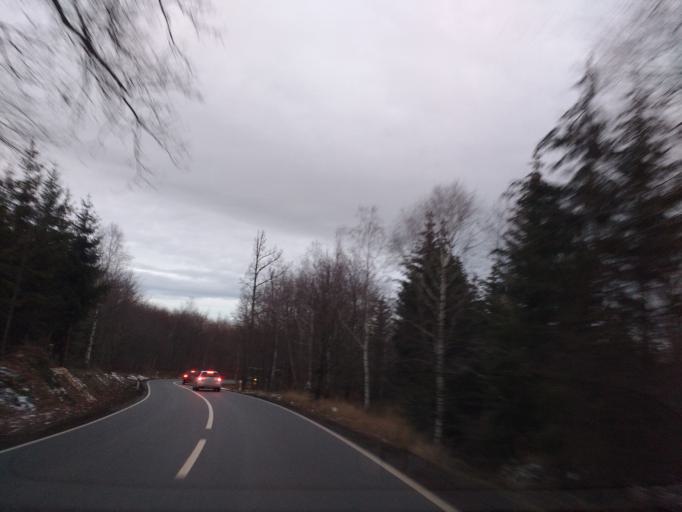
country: DE
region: Saxony-Anhalt
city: Friedrichsbrunn
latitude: 51.7096
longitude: 11.0720
